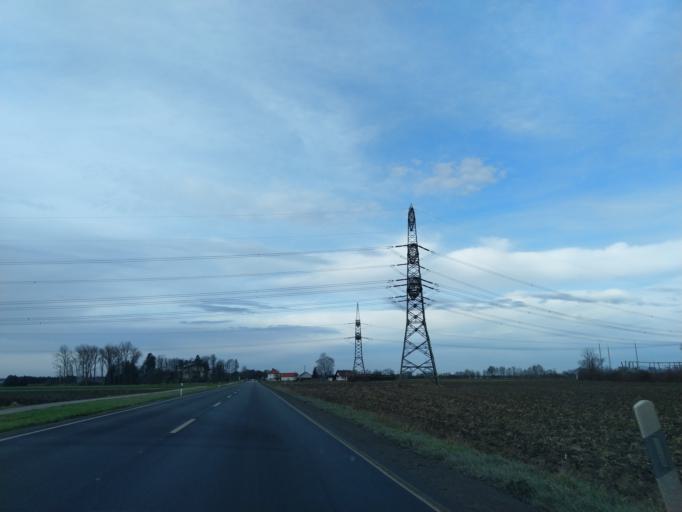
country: DE
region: Bavaria
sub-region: Lower Bavaria
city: Kunzing
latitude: 48.6652
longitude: 13.1018
